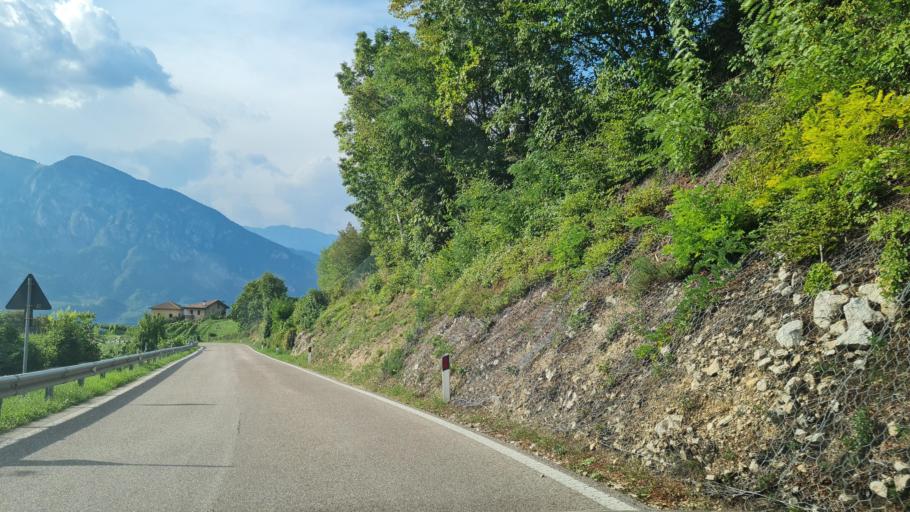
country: IT
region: Trentino-Alto Adige
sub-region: Provincia di Trento
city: Mattarello
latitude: 46.0113
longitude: 11.1497
